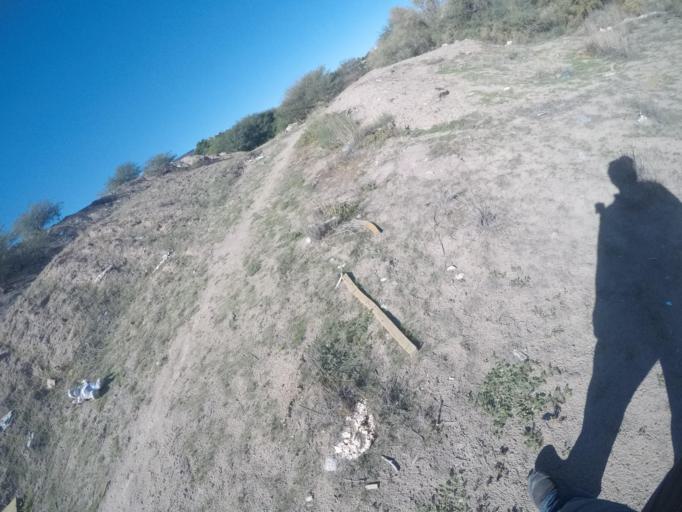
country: US
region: Texas
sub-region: El Paso County
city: Socorro
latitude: 31.6702
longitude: -106.4024
